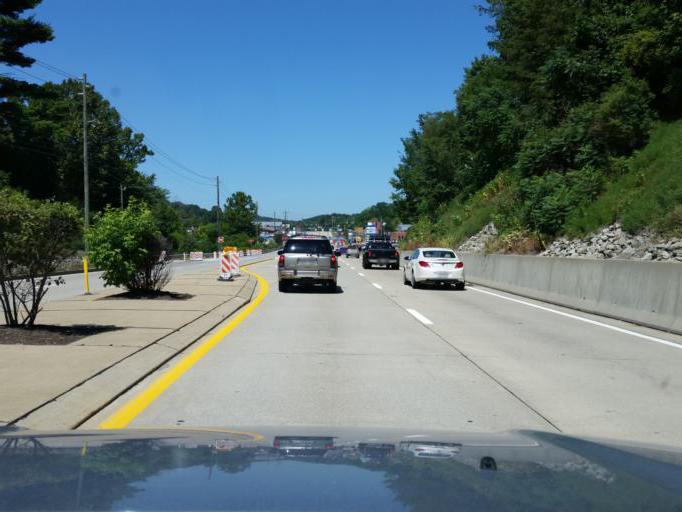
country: US
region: Pennsylvania
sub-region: Westmoreland County
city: Murrysville
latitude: 40.4209
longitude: -79.6571
